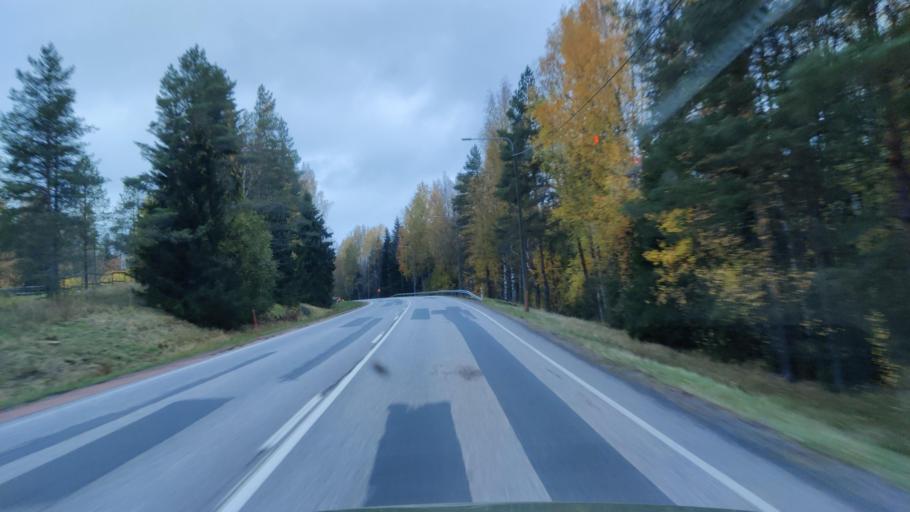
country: FI
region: Uusimaa
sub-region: Helsinki
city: Vihti
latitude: 60.3324
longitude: 24.2085
